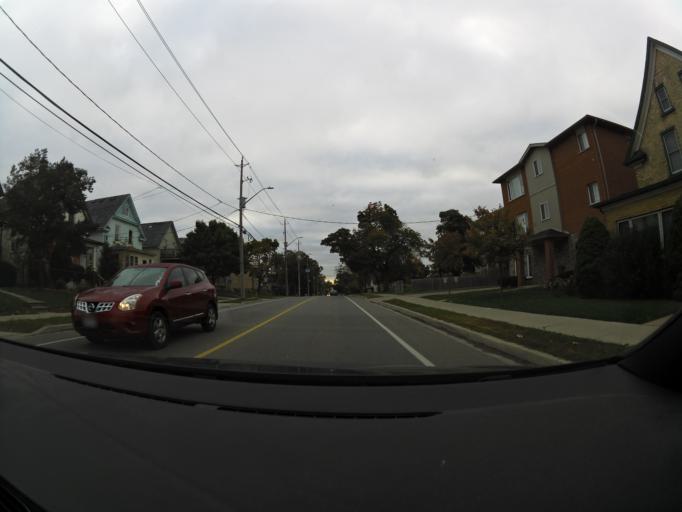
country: CA
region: Ontario
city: Kitchener
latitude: 43.4438
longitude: -80.4888
